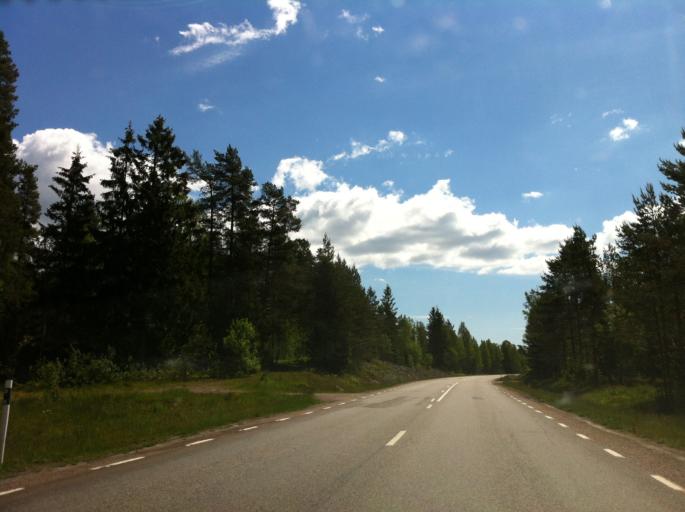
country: SE
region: Vaestra Goetaland
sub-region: Amals Kommun
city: Amal
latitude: 59.0247
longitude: 12.6774
